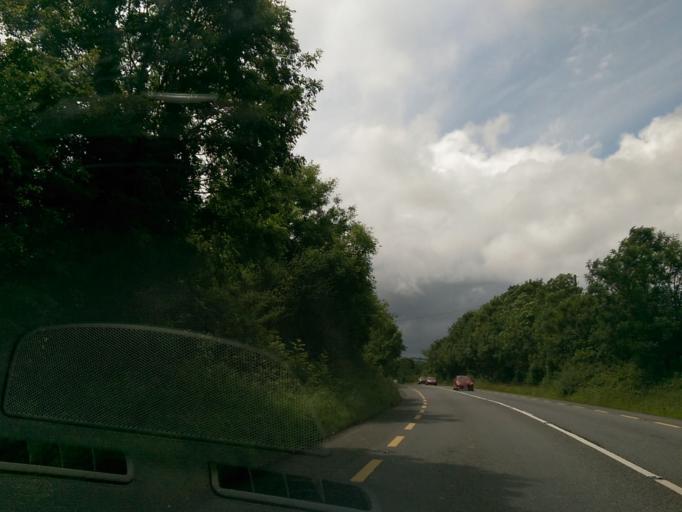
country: IE
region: Munster
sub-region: An Clar
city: Ennis
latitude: 52.7984
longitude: -9.0353
